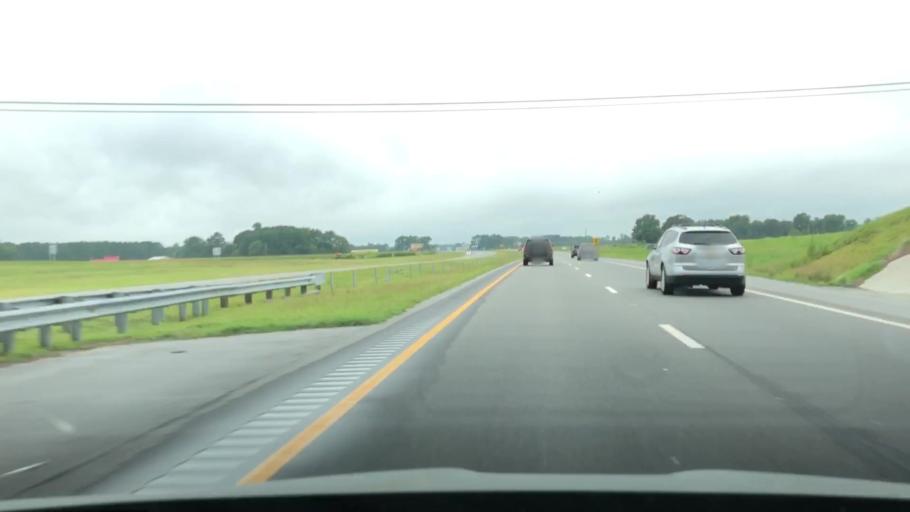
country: US
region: North Carolina
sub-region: Wayne County
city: Elroy
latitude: 35.4122
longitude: -77.8975
